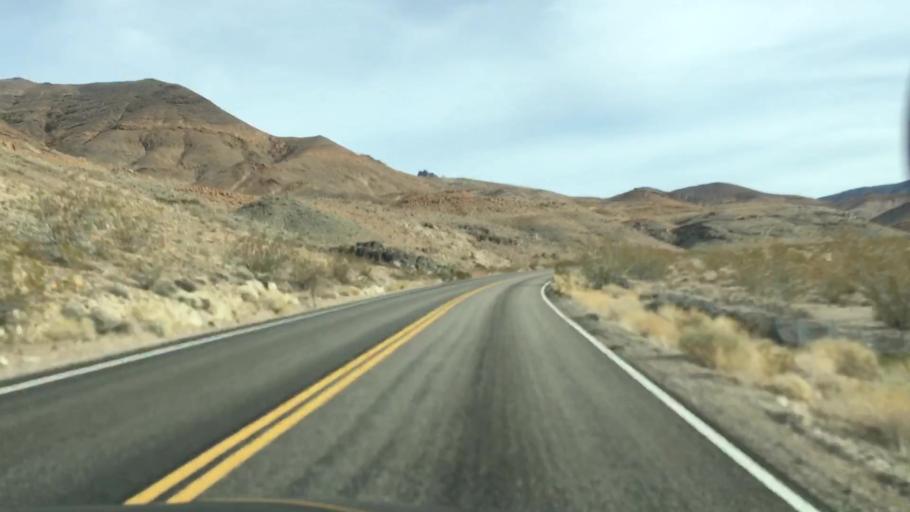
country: US
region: Nevada
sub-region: Nye County
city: Beatty
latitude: 36.7409
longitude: -116.9662
